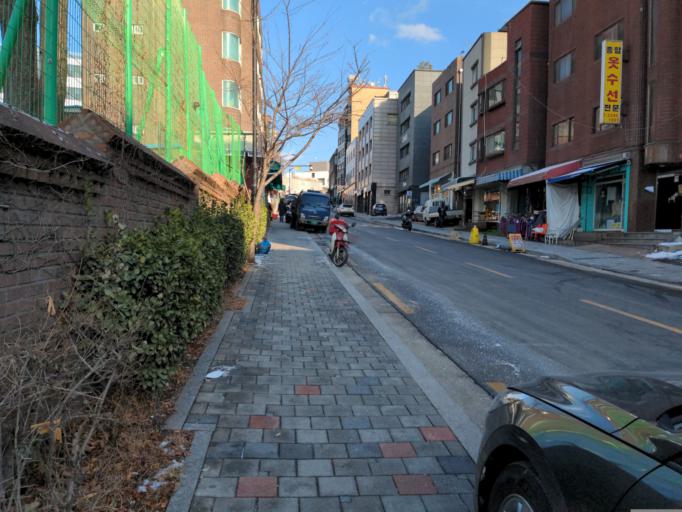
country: KR
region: Seoul
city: Seoul
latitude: 37.5607
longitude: 127.0430
